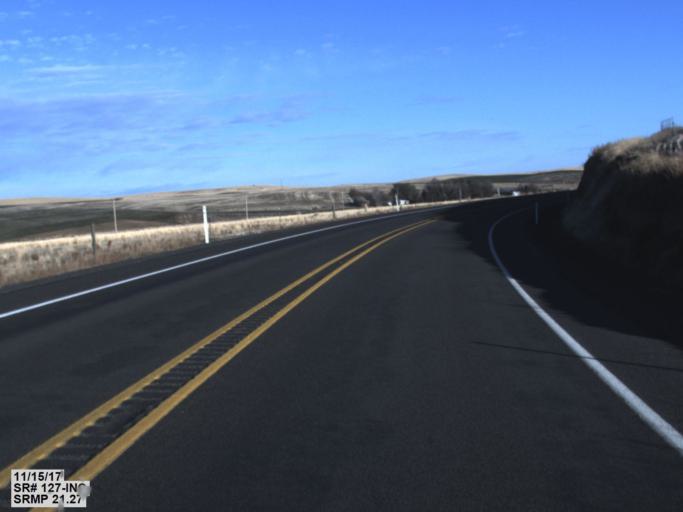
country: US
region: Washington
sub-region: Garfield County
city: Pomeroy
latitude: 46.7472
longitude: -117.7299
